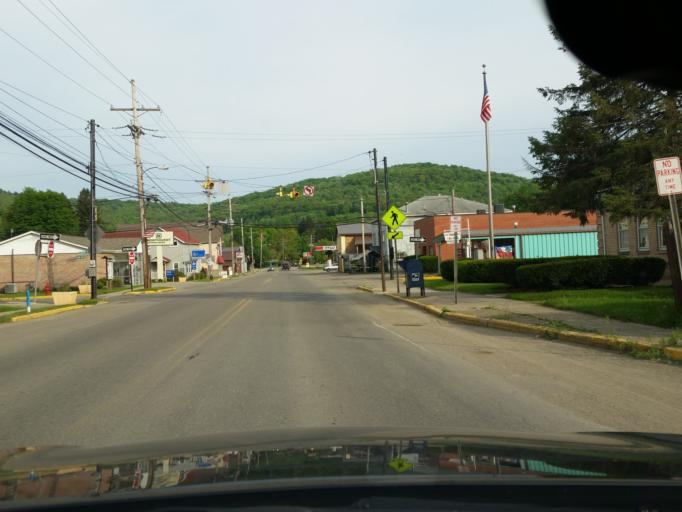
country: US
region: Pennsylvania
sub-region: Warren County
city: Sheffield
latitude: 41.7025
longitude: -79.0342
